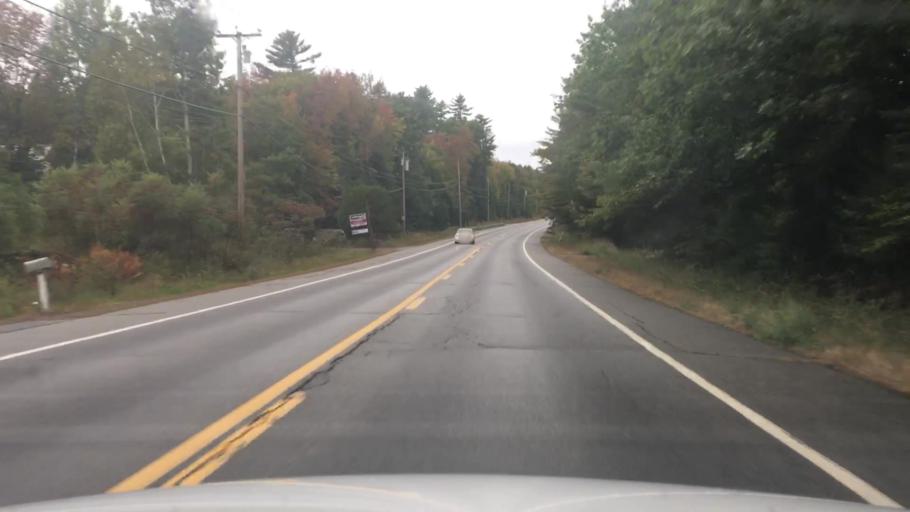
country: US
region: Maine
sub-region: Kennebec County
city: Rome
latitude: 44.5128
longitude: -69.8740
